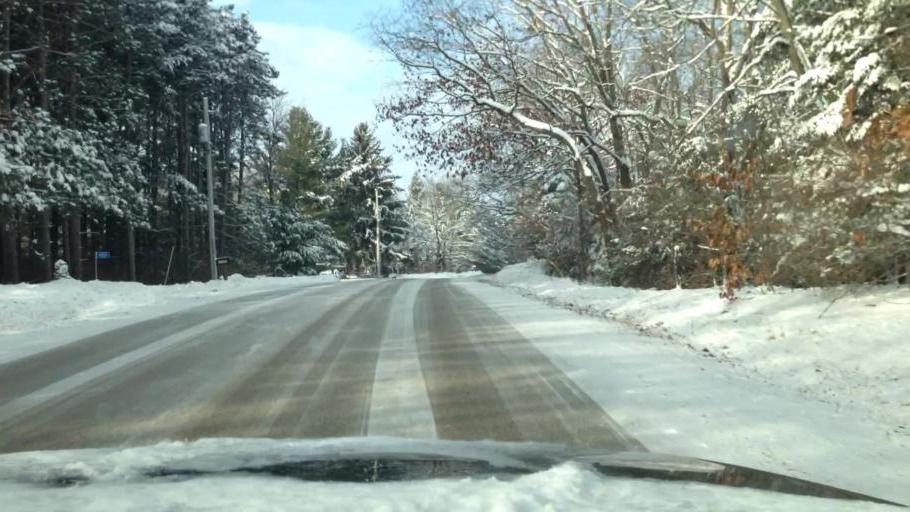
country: US
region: Wisconsin
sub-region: Walworth County
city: East Troy
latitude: 42.8116
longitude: -88.4268
